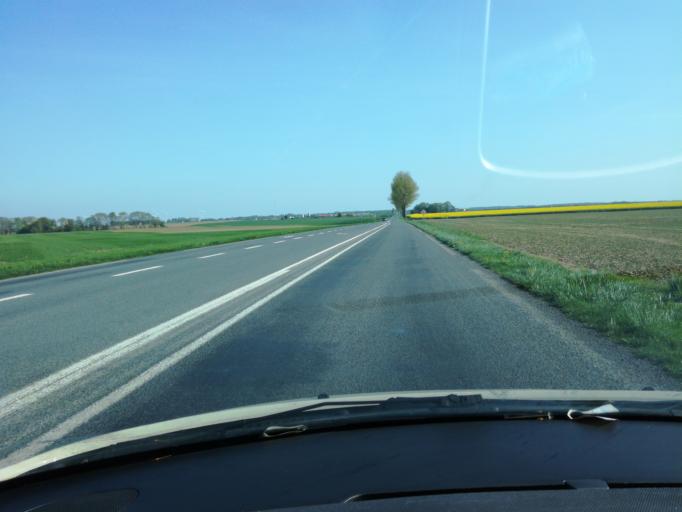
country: FR
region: Picardie
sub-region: Departement de la Somme
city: Poix-de-Picardie
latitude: 49.8209
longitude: 1.9559
